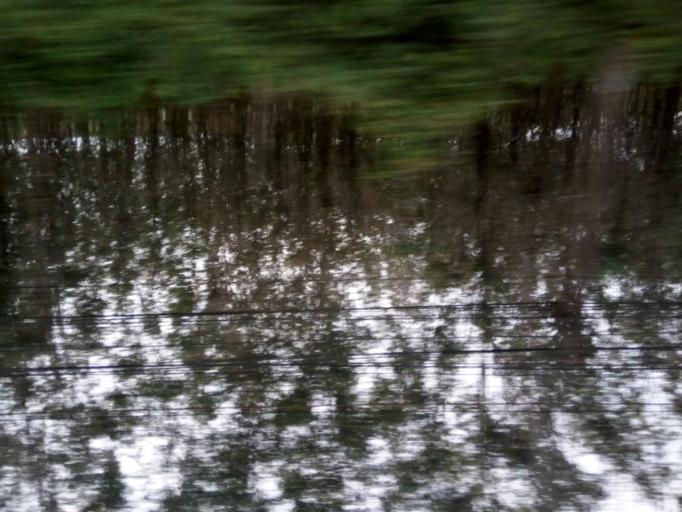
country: TH
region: Phuket
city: Thalang
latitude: 8.0585
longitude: 98.4039
